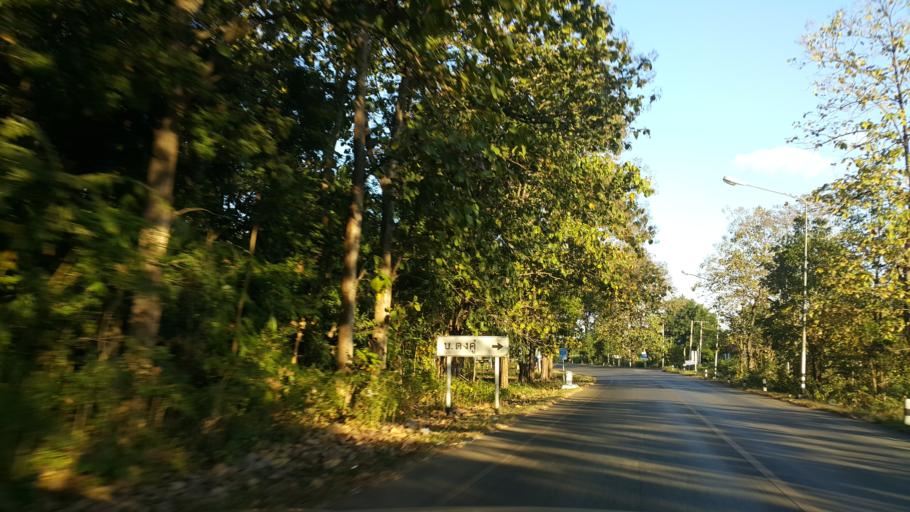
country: TH
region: Sukhothai
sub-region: Amphoe Si Satchanalai
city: Si Satchanalai
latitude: 17.5489
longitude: 99.8950
